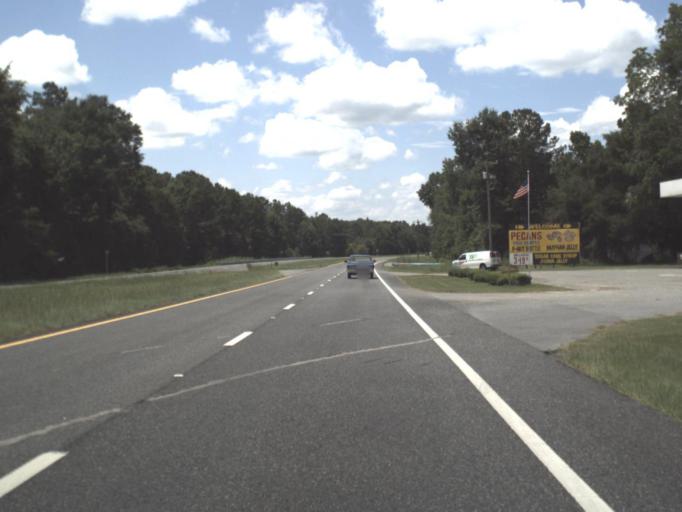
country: US
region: Florida
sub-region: Jefferson County
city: Monticello
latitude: 30.3460
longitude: -83.7903
